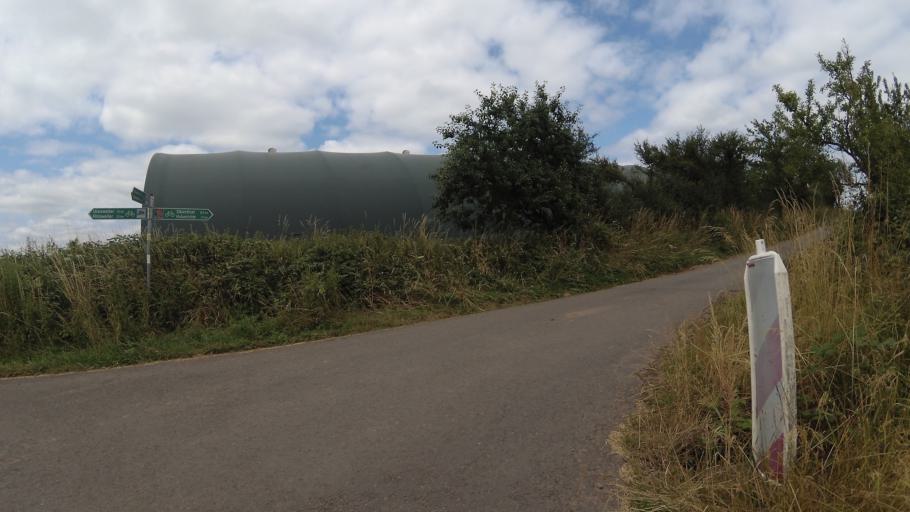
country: DE
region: Saarland
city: Mainzweiler
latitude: 49.4193
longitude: 7.1022
